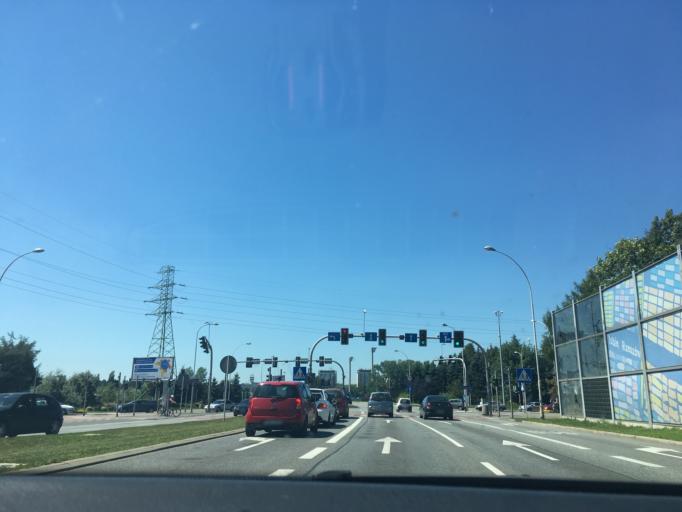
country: PL
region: Subcarpathian Voivodeship
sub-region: Rzeszow
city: Rzeszow
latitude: 50.0197
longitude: 22.0048
